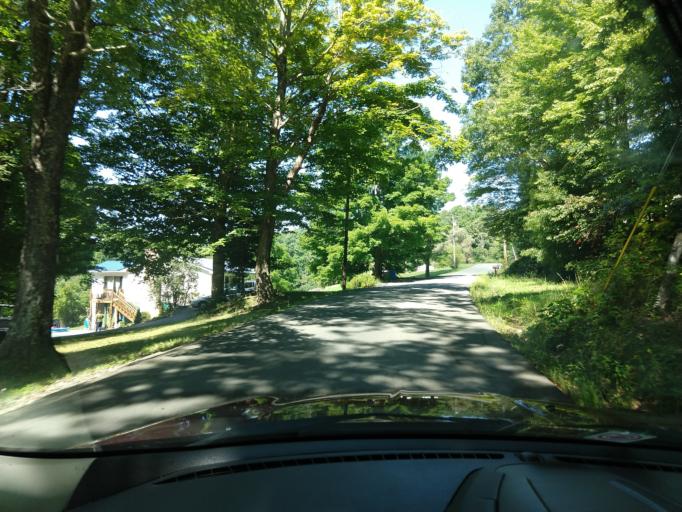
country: US
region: West Virginia
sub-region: Nicholas County
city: Craigsville
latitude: 38.2811
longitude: -80.7341
